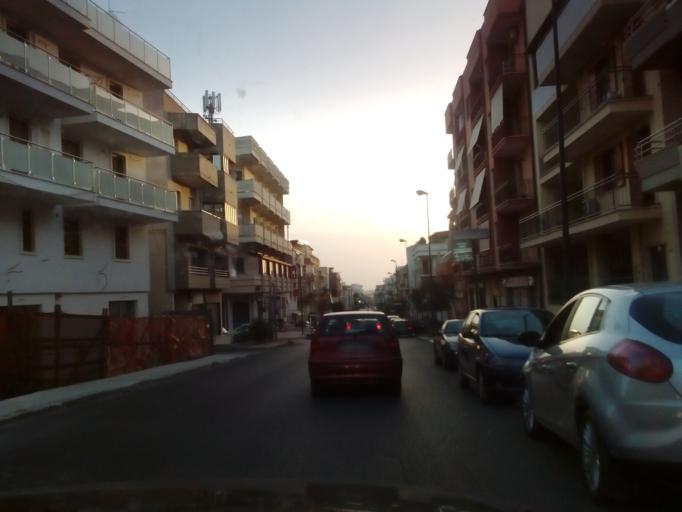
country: IT
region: Apulia
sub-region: Provincia di Bari
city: Gravina in Puglia
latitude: 40.8181
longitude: 16.4308
